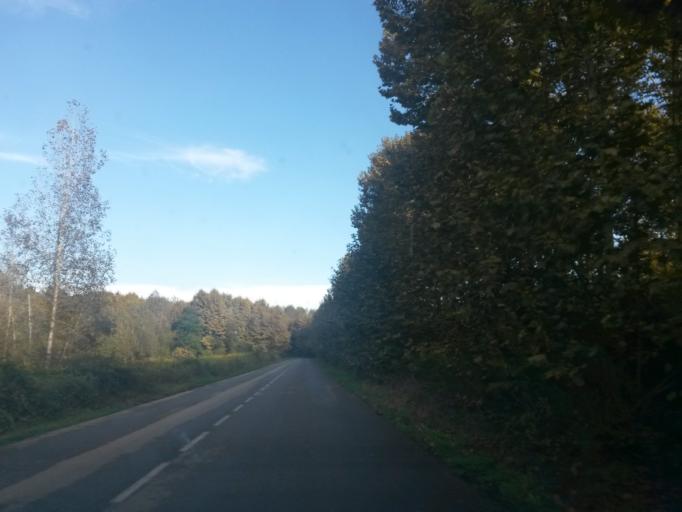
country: ES
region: Catalonia
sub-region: Provincia de Girona
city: Angles
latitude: 41.9633
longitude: 2.6559
